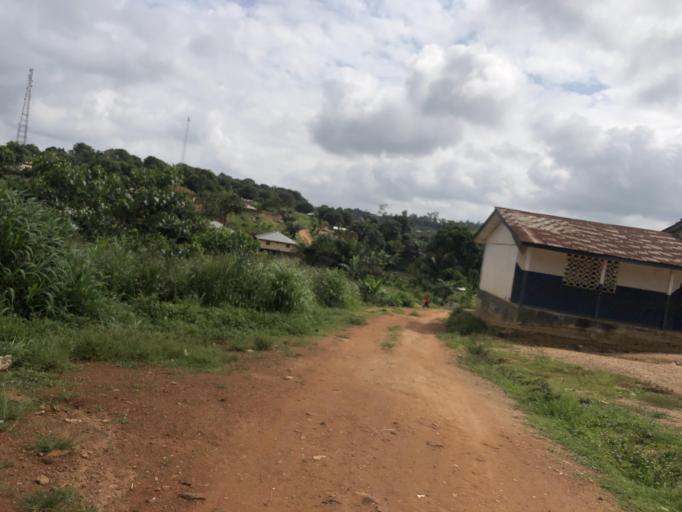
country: SL
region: Eastern Province
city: Kailahun
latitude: 8.2784
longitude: -10.5660
